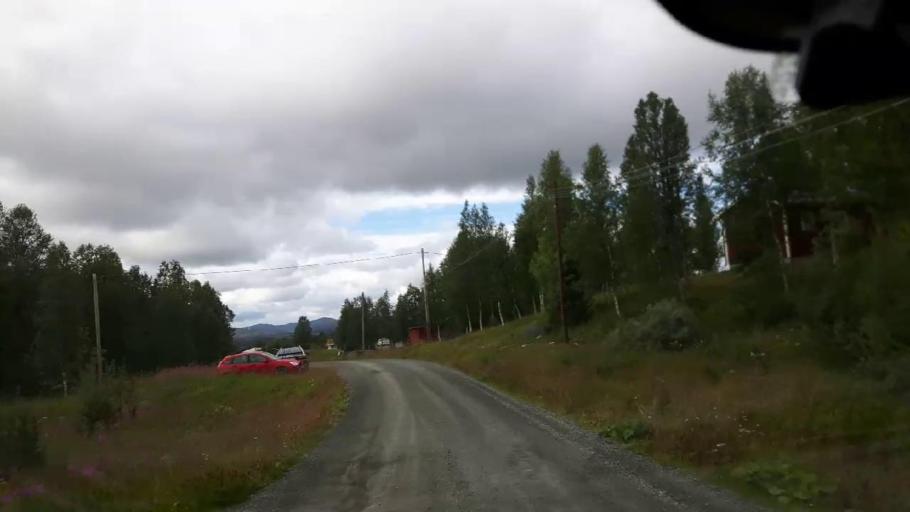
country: SE
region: Jaemtland
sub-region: Krokoms Kommun
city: Valla
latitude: 63.7803
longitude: 13.8242
